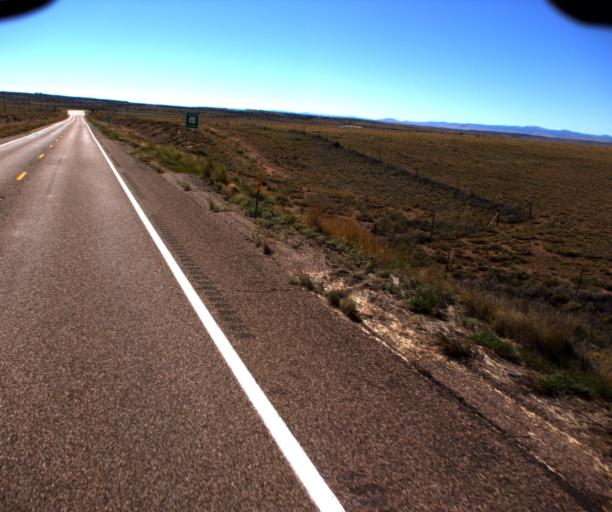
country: US
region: Arizona
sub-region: Apache County
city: Saint Johns
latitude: 34.5174
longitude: -109.4513
